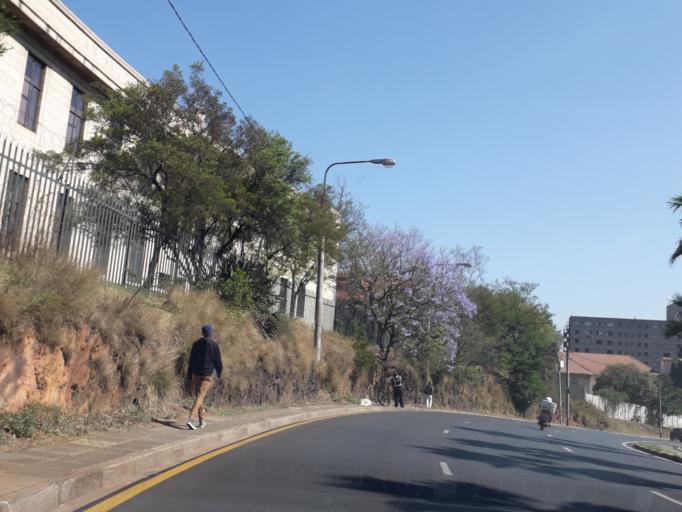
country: ZA
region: Gauteng
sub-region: City of Johannesburg Metropolitan Municipality
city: Johannesburg
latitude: -26.1908
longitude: 28.0322
